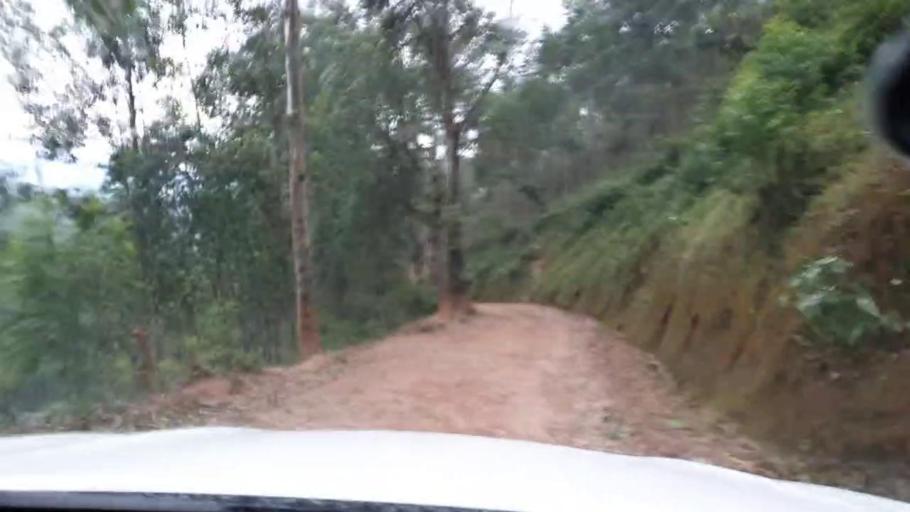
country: RW
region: Western Province
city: Cyangugu
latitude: -2.4103
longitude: 29.1989
